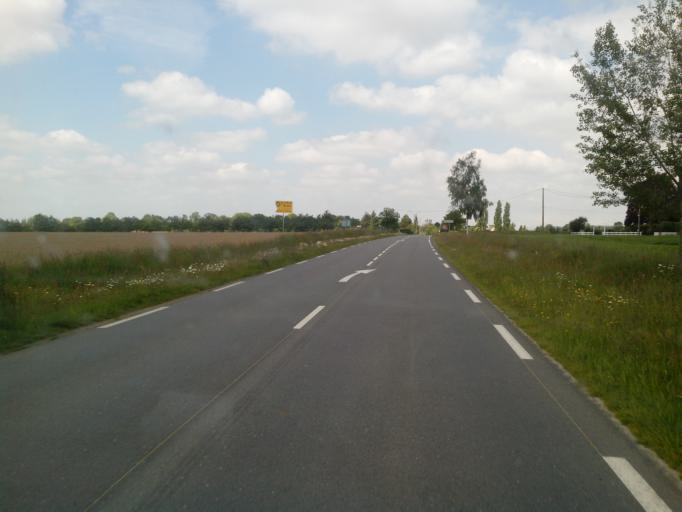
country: FR
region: Brittany
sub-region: Departement d'Ille-et-Vilaine
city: Lecousse
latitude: 48.3693
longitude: -1.2382
